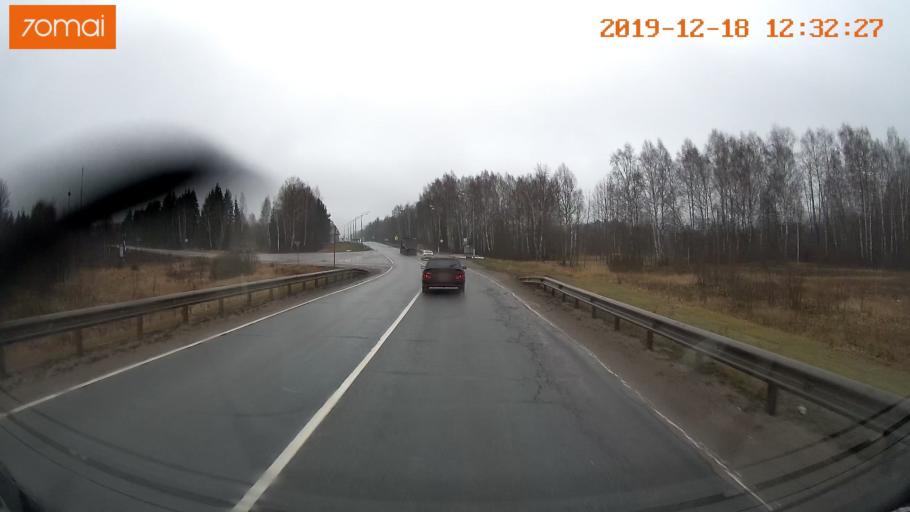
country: RU
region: Moskovskaya
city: Rumyantsevo
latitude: 56.1058
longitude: 36.5510
